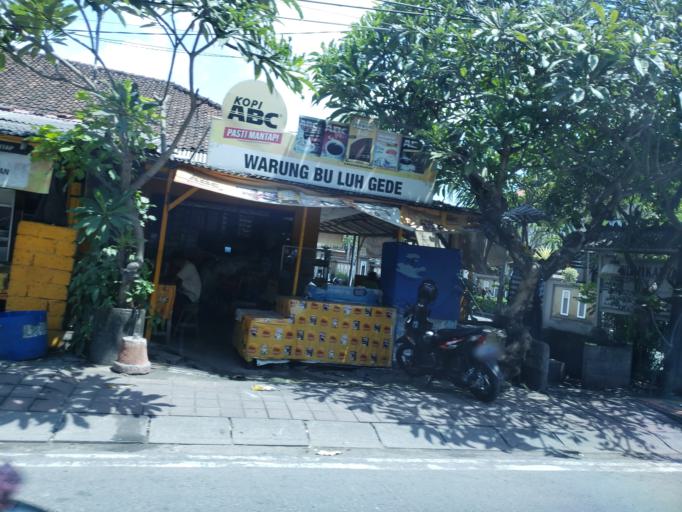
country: ID
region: Bali
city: Kelanabian
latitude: -8.7719
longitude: 115.1729
